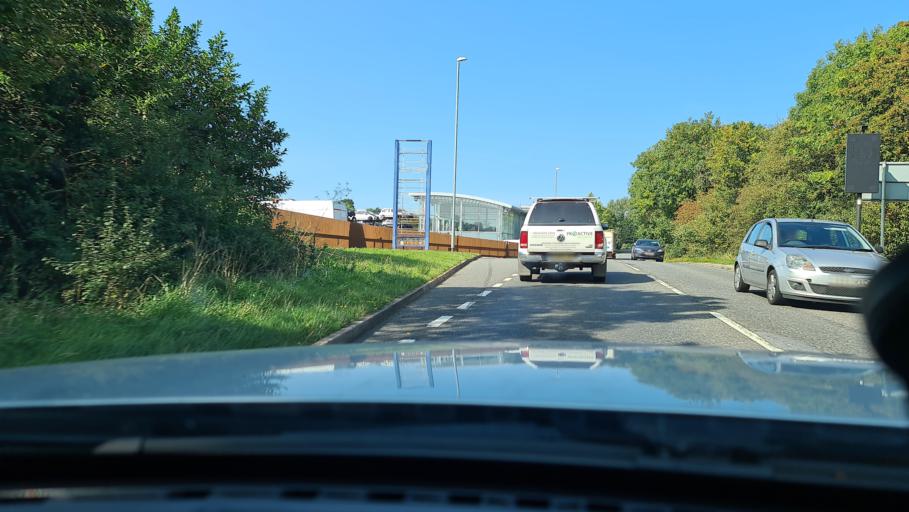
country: GB
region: England
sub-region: Northamptonshire
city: Daventry
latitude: 52.2457
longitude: -1.1466
